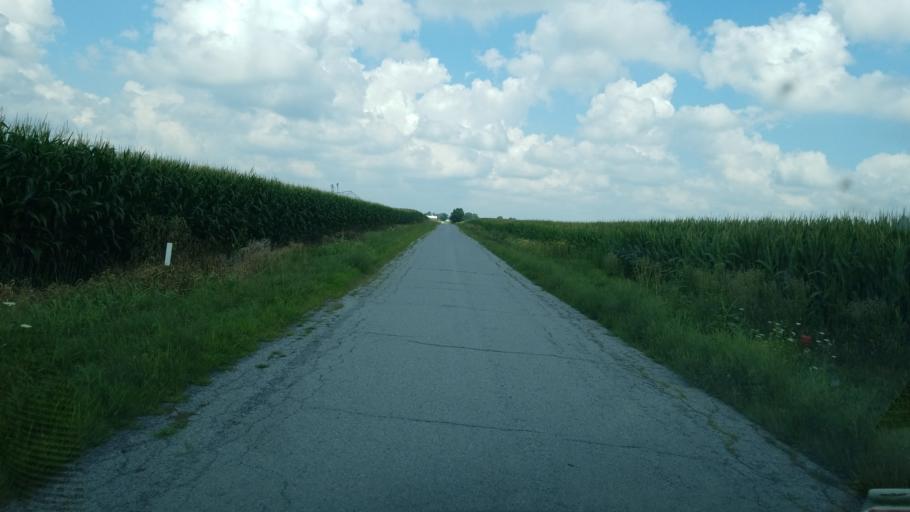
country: US
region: Ohio
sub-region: Crawford County
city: Bucyrus
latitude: 40.7057
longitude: -83.0381
